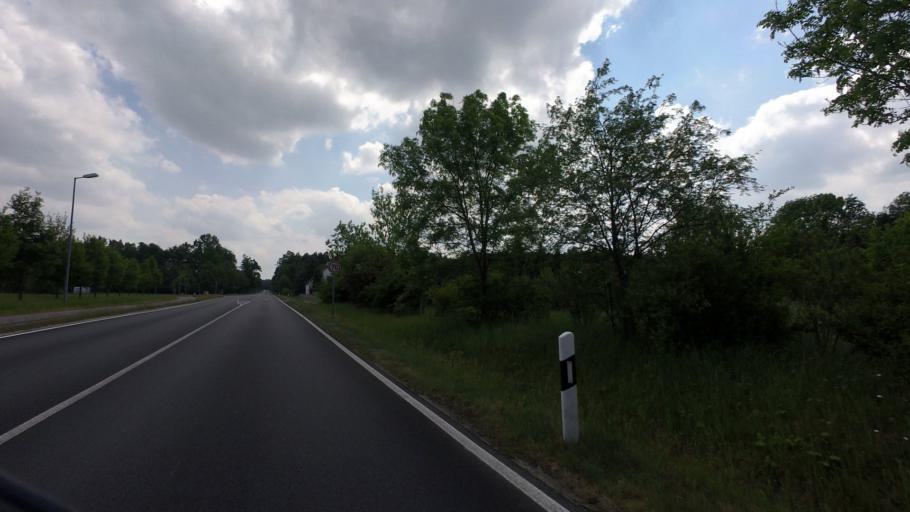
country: DE
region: Saxony
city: Rietschen
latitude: 51.3838
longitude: 14.7873
